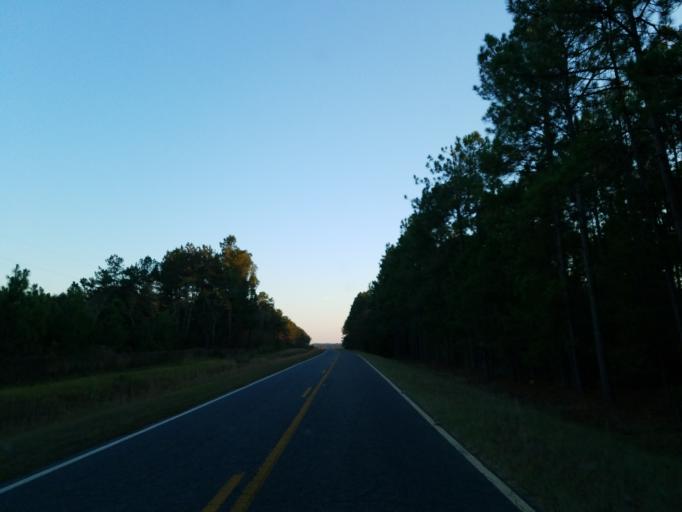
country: US
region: Georgia
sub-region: Ben Hill County
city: Fitzgerald
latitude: 31.7001
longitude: -83.4166
